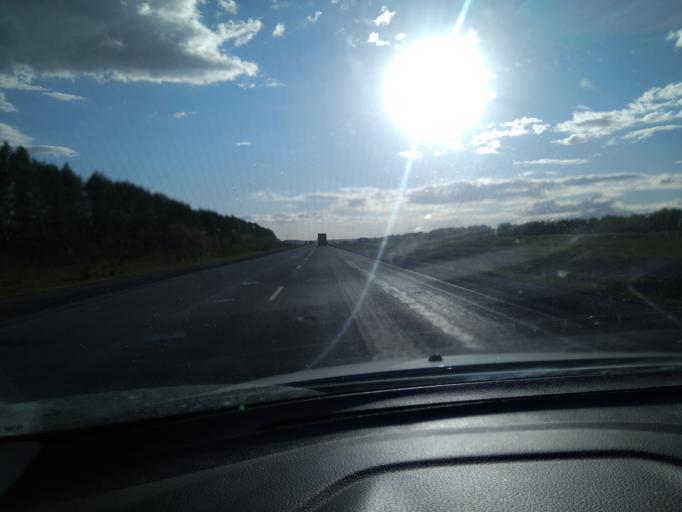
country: RU
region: Sverdlovsk
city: Troitskiy
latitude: 57.0855
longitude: 63.6863
